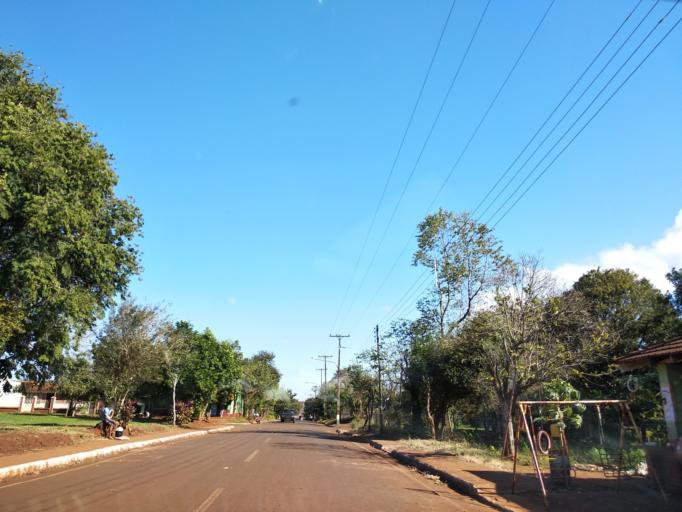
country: PY
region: Itapua
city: Hohenau
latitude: -27.0555
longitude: -55.7423
